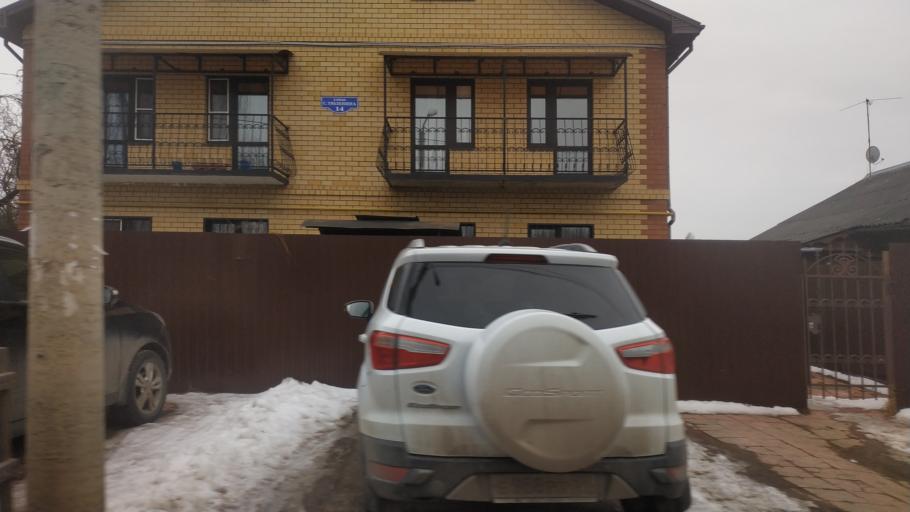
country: RU
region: Tverskaya
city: Tver
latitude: 56.8825
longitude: 35.8847
